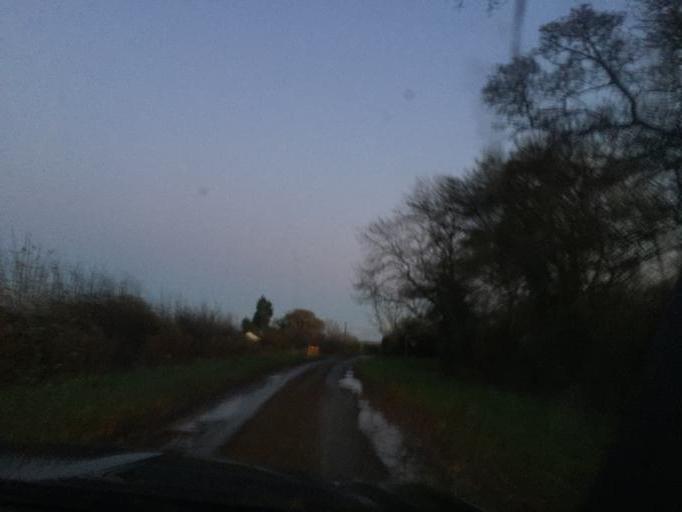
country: GB
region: England
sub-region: Northamptonshire
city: Silverstone
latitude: 52.0889
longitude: -1.0965
